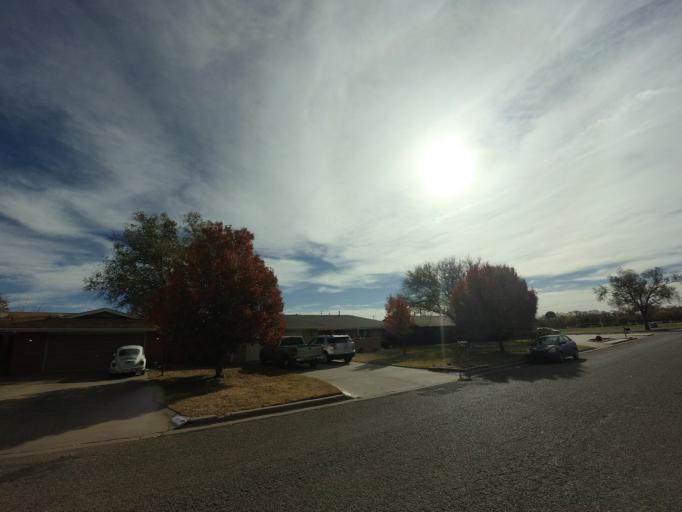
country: US
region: New Mexico
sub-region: Curry County
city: Clovis
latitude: 34.4127
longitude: -103.1810
